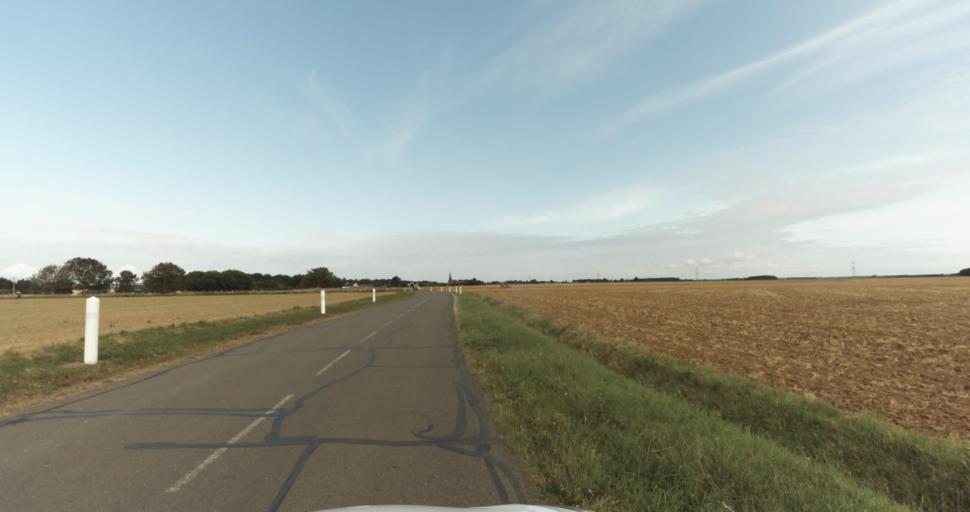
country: FR
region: Haute-Normandie
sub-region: Departement de l'Eure
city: La Madeleine-de-Nonancourt
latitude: 48.8390
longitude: 1.1710
